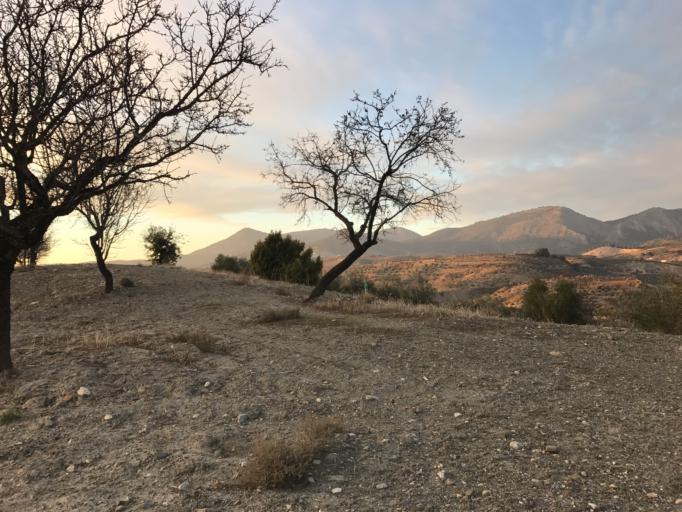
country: ES
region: Andalusia
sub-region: Provincia de Granada
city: Beas de Granada
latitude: 37.2111
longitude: -3.4856
